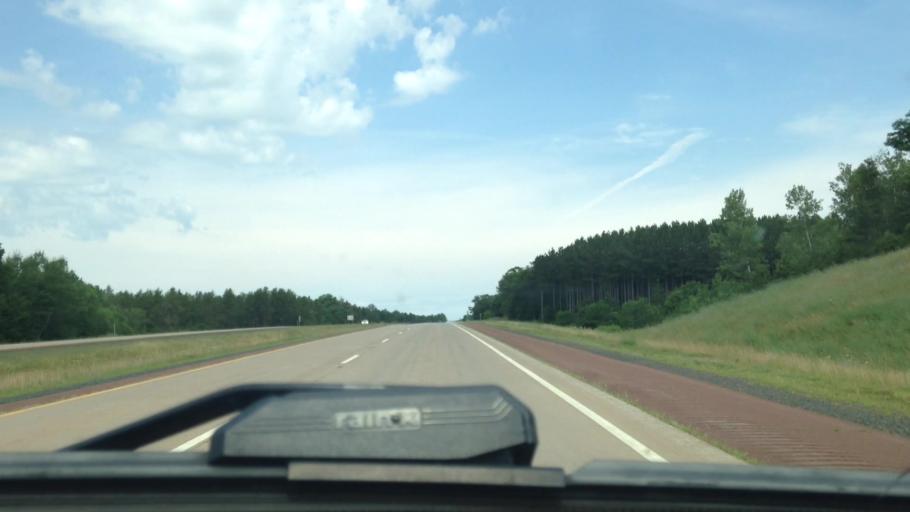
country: US
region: Wisconsin
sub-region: Douglas County
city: Lake Nebagamon
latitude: 46.3317
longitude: -91.8248
